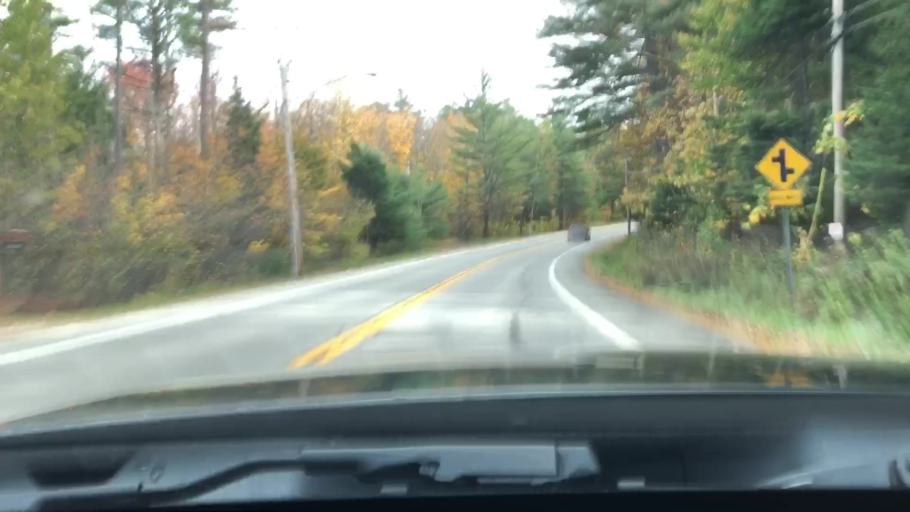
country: US
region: New York
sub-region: Hamilton County
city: Lake Pleasant
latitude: 43.4412
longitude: -74.4751
